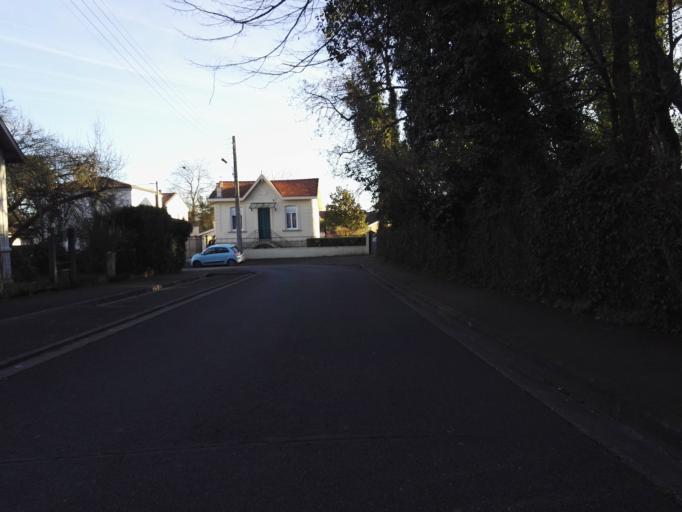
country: FR
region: Aquitaine
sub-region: Departement de la Gironde
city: Merignac
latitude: 44.8207
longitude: -0.6157
